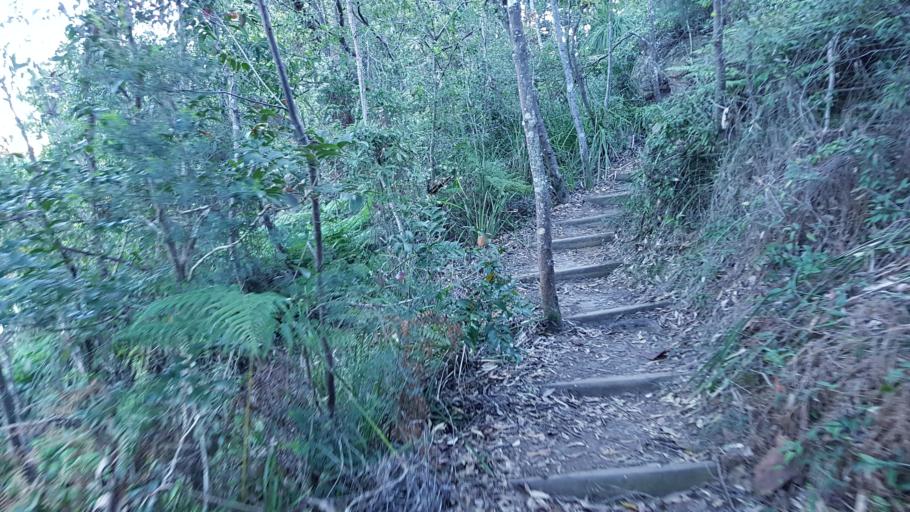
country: AU
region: New South Wales
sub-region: Ryde
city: East Ryde
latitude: -33.7996
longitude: 151.1443
